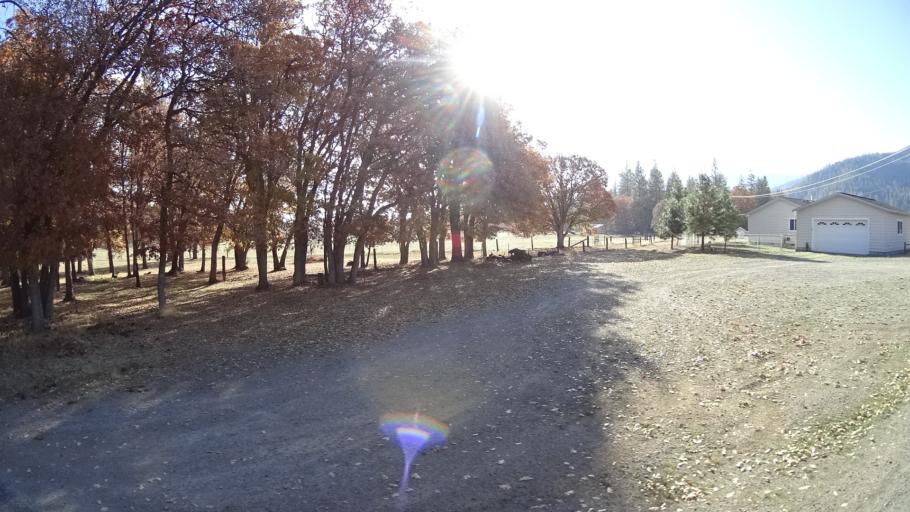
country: US
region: California
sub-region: Siskiyou County
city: Yreka
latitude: 41.6817
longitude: -122.6418
